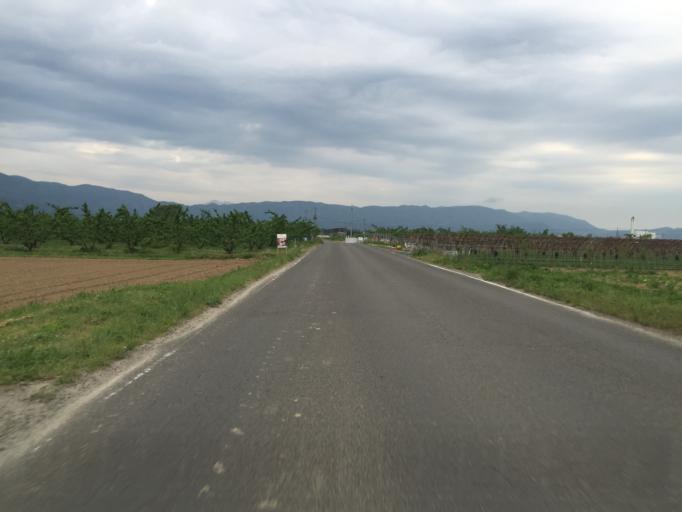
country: JP
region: Fukushima
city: Hobaramachi
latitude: 37.8296
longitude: 140.5382
